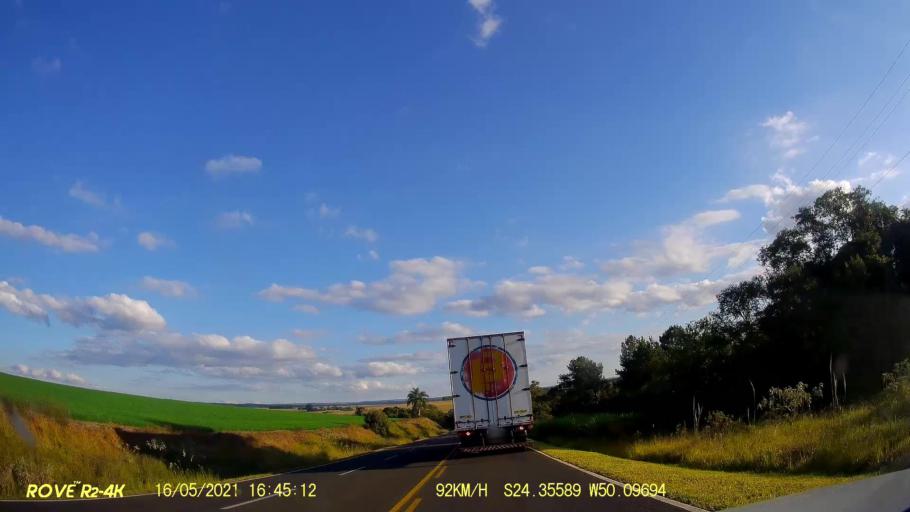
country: BR
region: Parana
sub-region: Pirai Do Sul
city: Pirai do Sul
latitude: -24.3560
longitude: -50.0965
